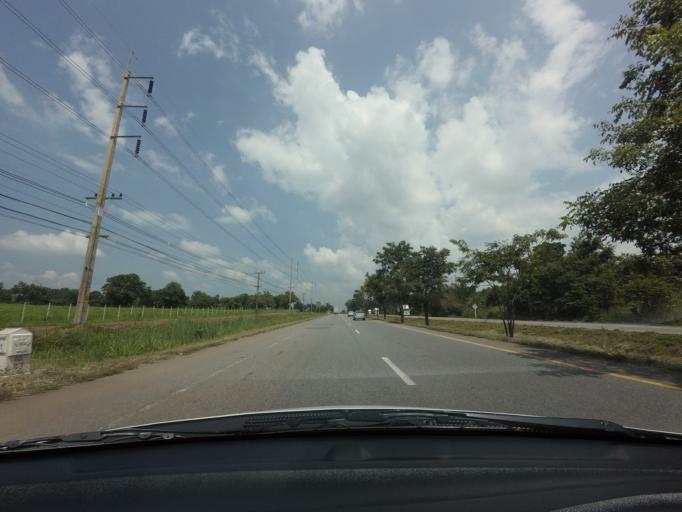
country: TH
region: Prachin Buri
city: Kabin Buri
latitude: 13.9284
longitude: 101.6882
